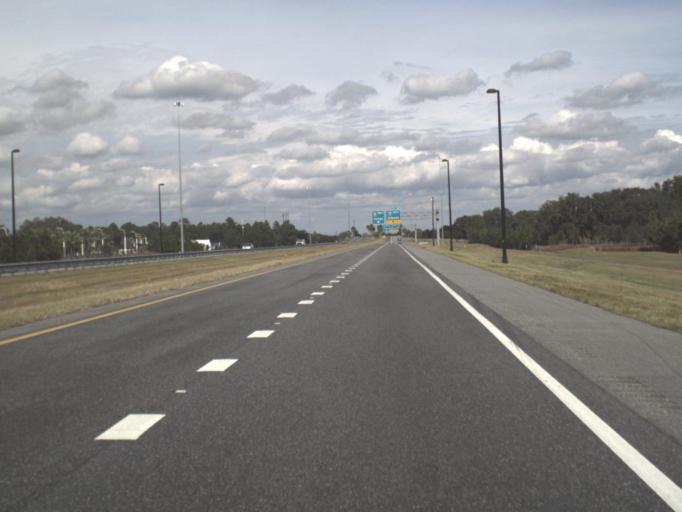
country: US
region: Florida
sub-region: Polk County
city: Polk City
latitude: 28.1464
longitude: -81.8437
